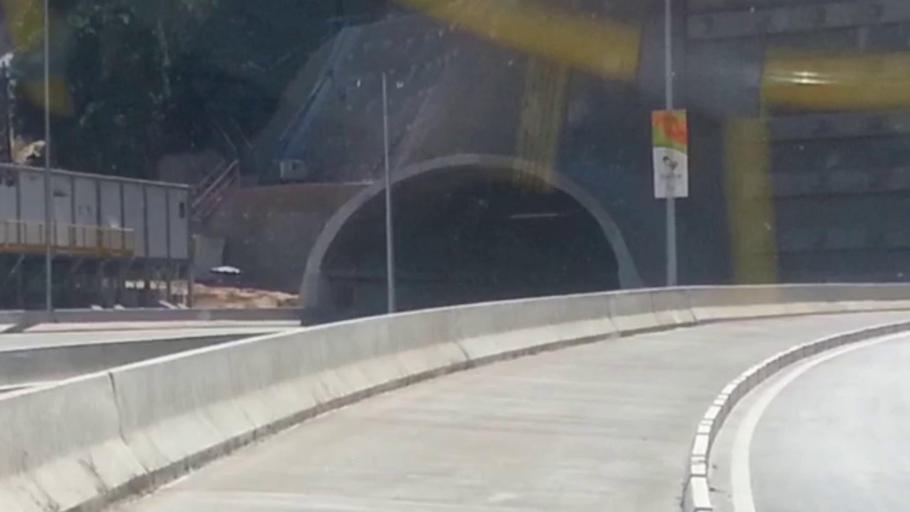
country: BR
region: Rio de Janeiro
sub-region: Nilopolis
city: Nilopolis
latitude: -22.9121
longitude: -43.4007
